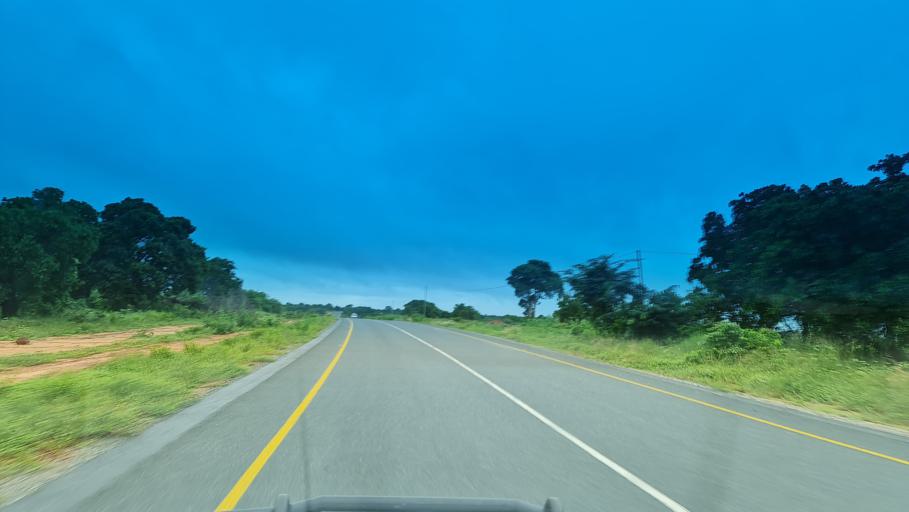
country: MZ
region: Nampula
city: Nampula
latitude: -15.6068
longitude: 39.3283
